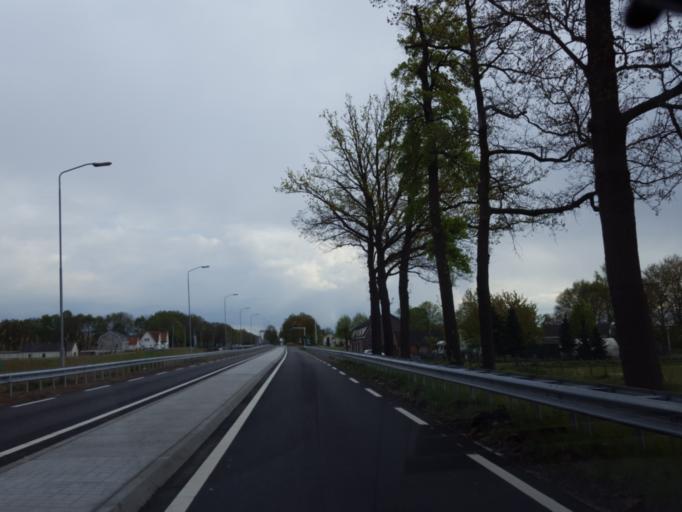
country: NL
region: North Brabant
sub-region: Gemeente Someren
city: Someren
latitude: 51.3542
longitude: 5.7424
